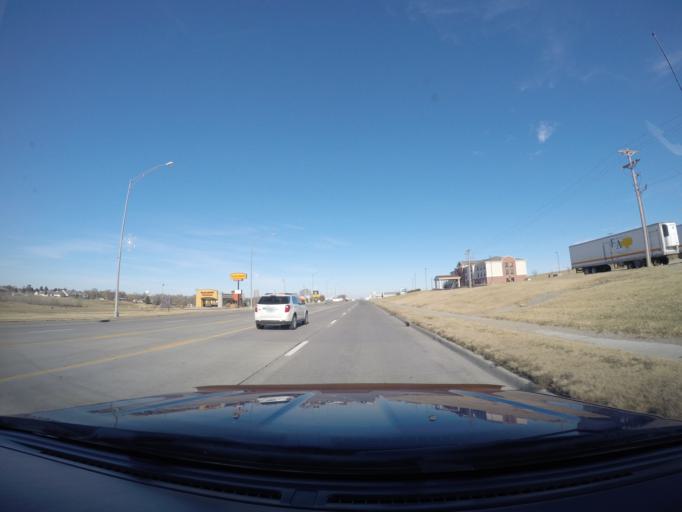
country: US
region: Kansas
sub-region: Cloud County
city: Concordia
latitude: 39.5546
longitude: -97.6573
